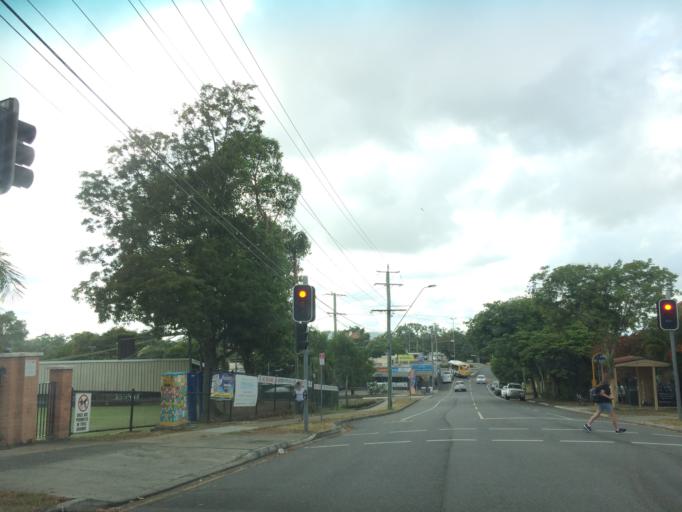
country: AU
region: Queensland
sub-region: Brisbane
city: Toowong
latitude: -27.5008
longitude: 152.9958
